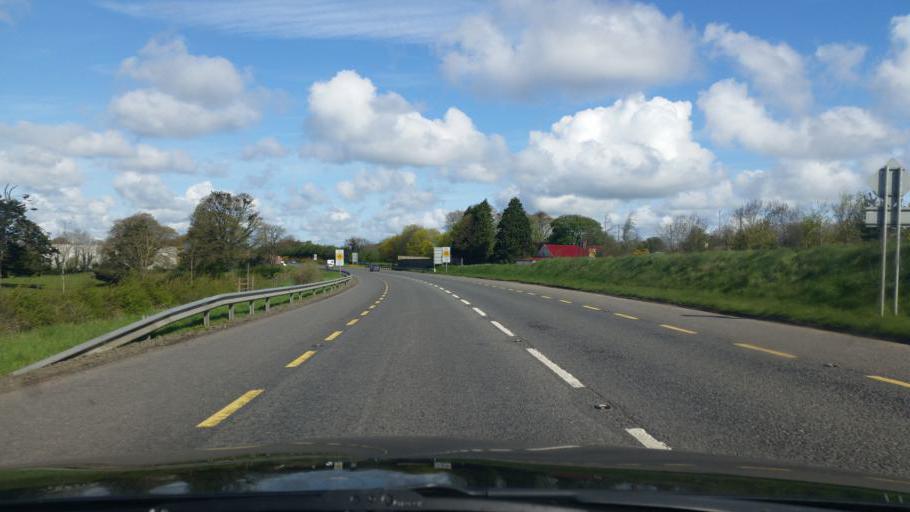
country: IE
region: Ulster
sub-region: An Cabhan
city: Mullagh
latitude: 53.7716
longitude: -6.9972
